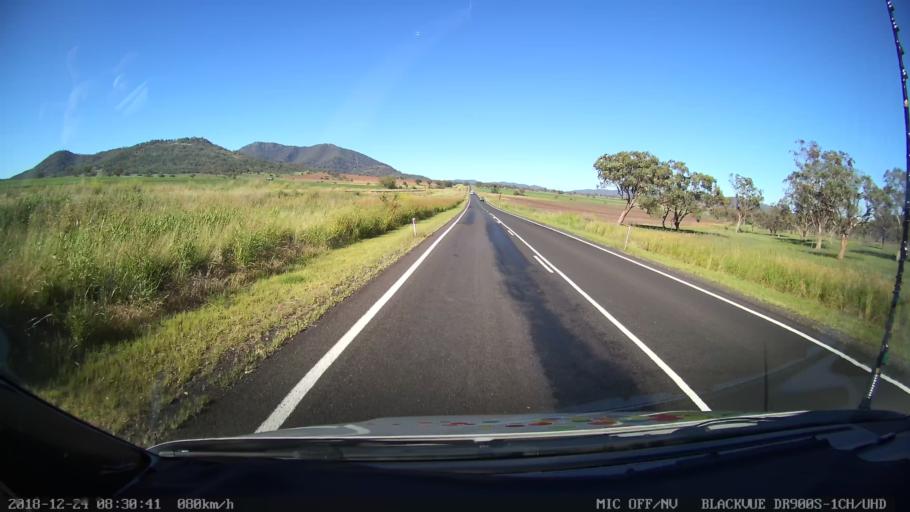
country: AU
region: New South Wales
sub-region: Tamworth Municipality
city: Phillip
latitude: -31.2689
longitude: 150.7215
